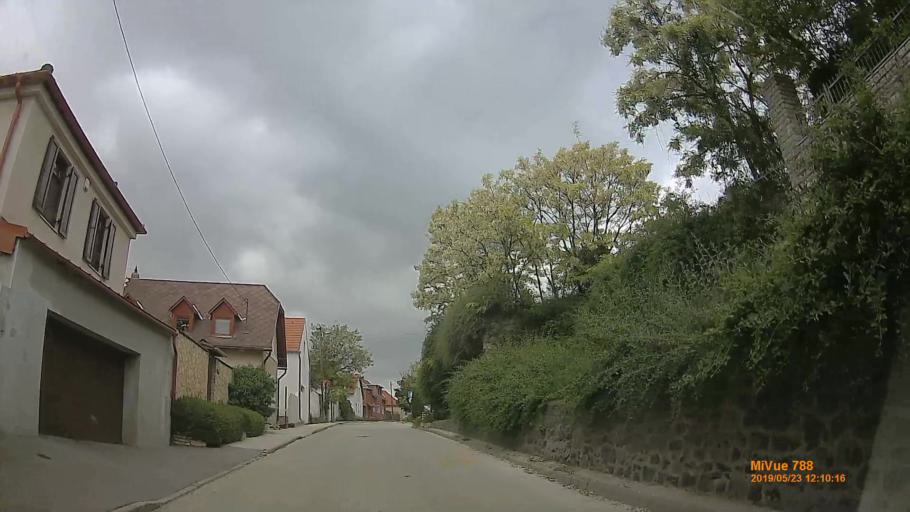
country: HU
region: Veszprem
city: Veszprem
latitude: 47.0989
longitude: 17.9053
